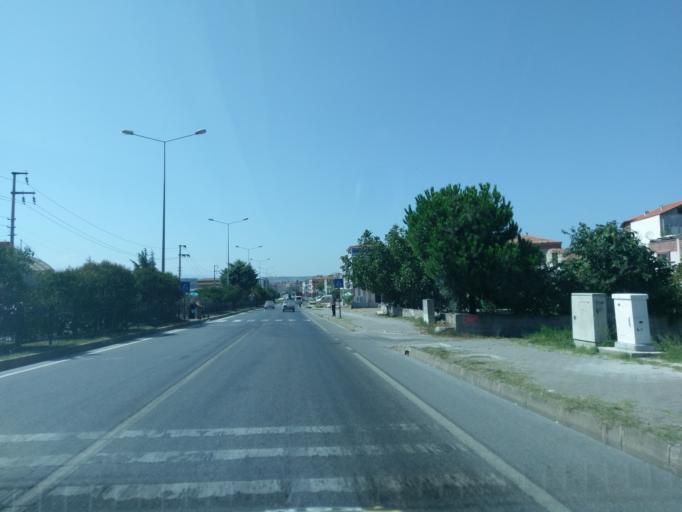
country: TR
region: Samsun
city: Bafra
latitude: 41.5570
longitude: 35.9084
